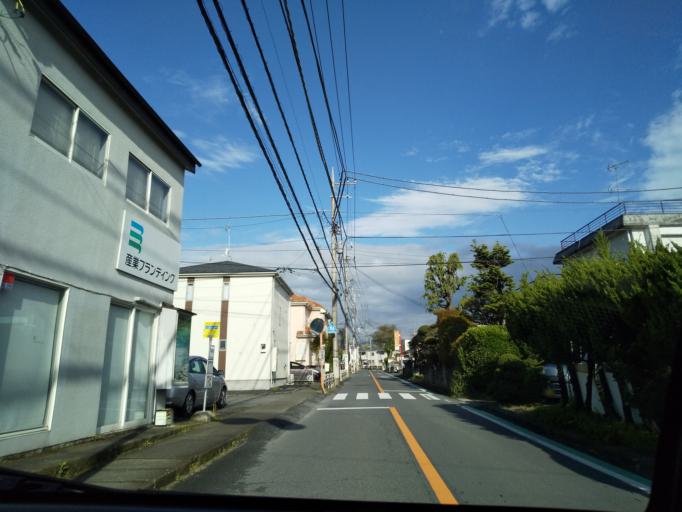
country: JP
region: Tokyo
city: Hachioji
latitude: 35.6726
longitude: 139.2897
